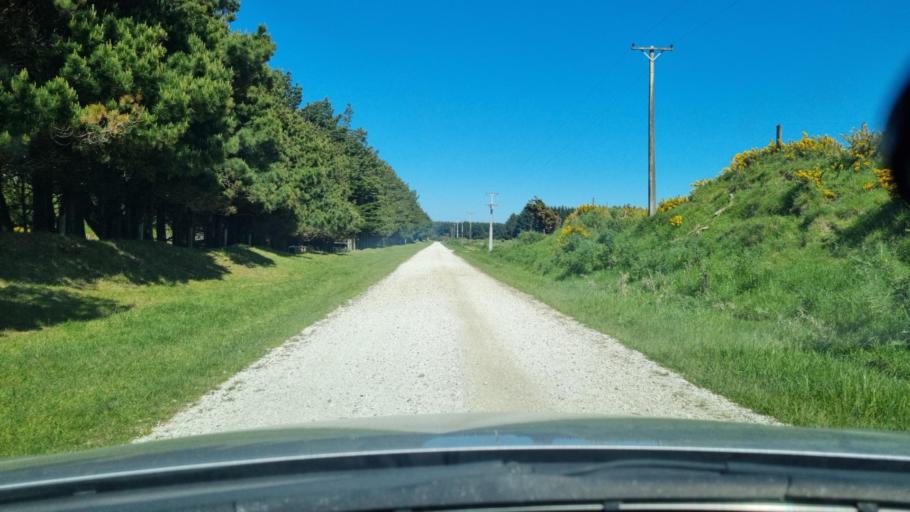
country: NZ
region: Southland
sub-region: Invercargill City
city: Invercargill
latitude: -46.4554
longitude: 168.2746
